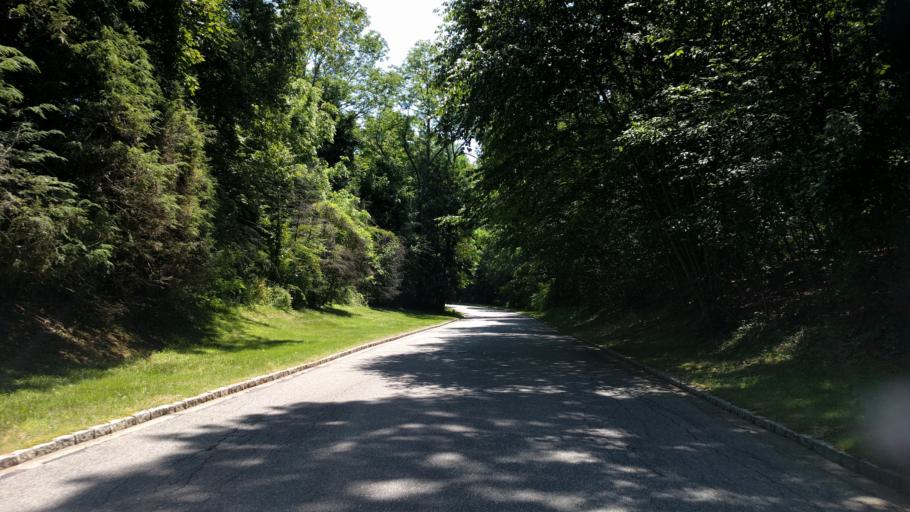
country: US
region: New York
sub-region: Nassau County
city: Oyster Bay
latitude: 40.8634
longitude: -73.5414
